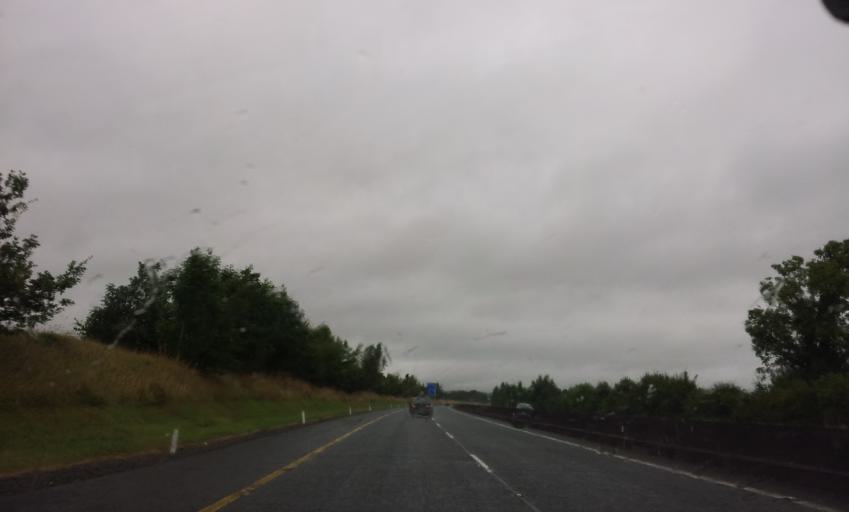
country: IE
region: Munster
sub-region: County Cork
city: Fermoy
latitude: 52.1483
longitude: -8.2660
